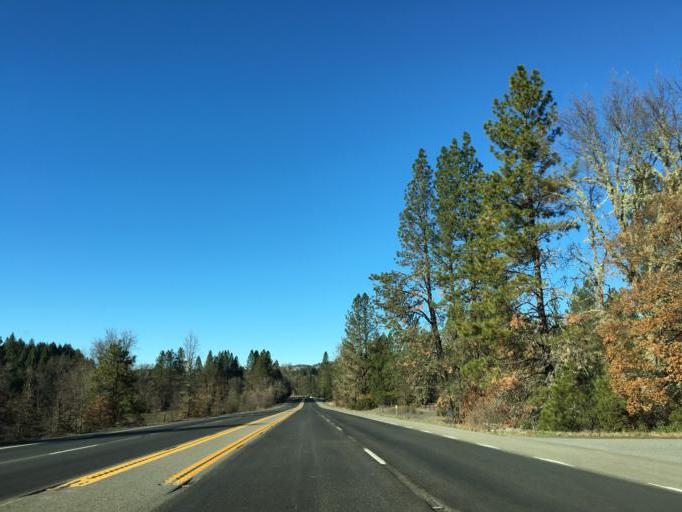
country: US
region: California
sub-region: Mendocino County
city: Laytonville
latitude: 39.7218
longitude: -123.5020
